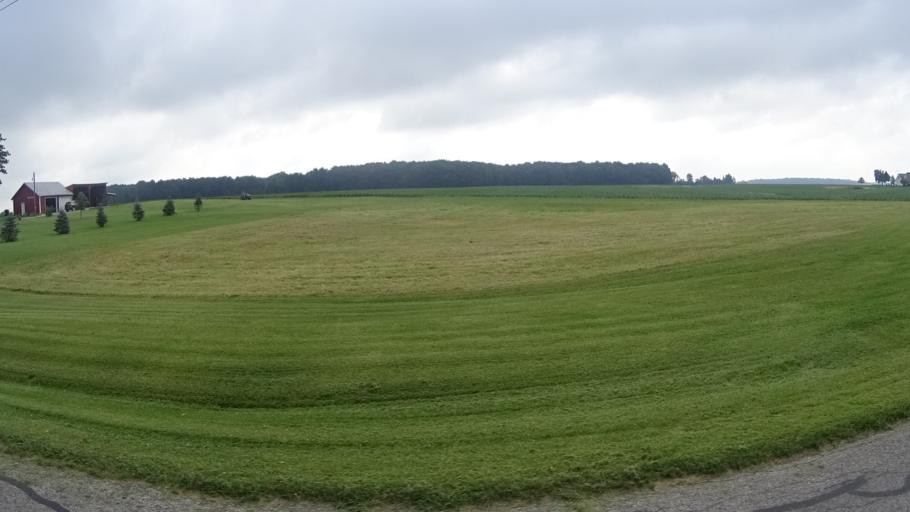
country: US
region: Ohio
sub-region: Erie County
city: Milan
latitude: 41.2876
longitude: -82.5117
